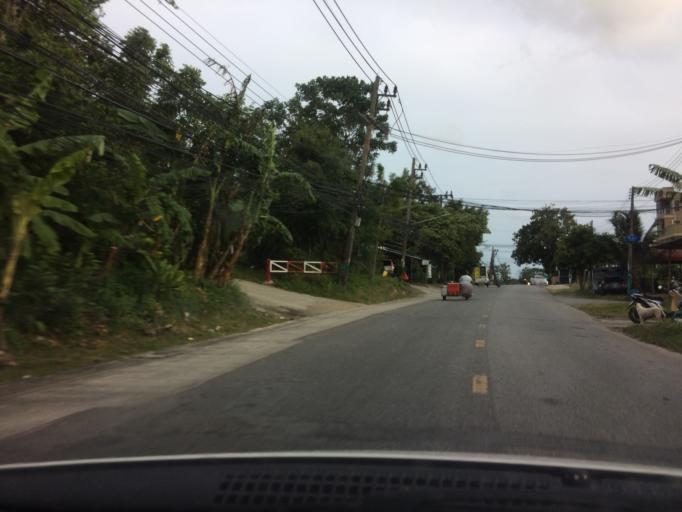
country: TH
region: Phuket
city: Phuket
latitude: 7.8937
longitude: 98.4073
